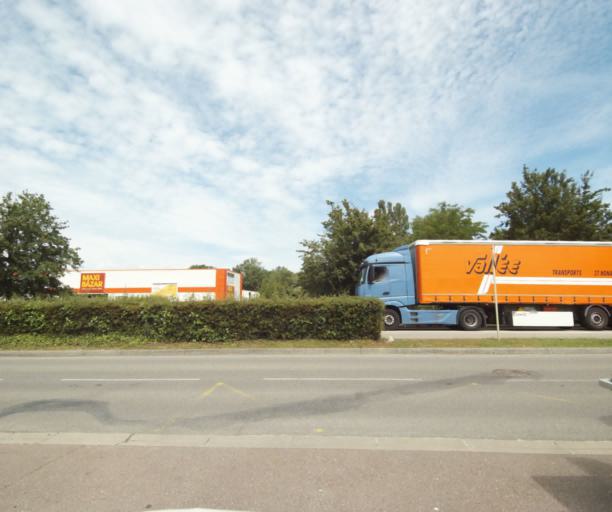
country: FR
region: Rhone-Alpes
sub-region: Departement de la Haute-Savoie
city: Anthy-sur-Leman
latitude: 46.3520
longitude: 6.4389
